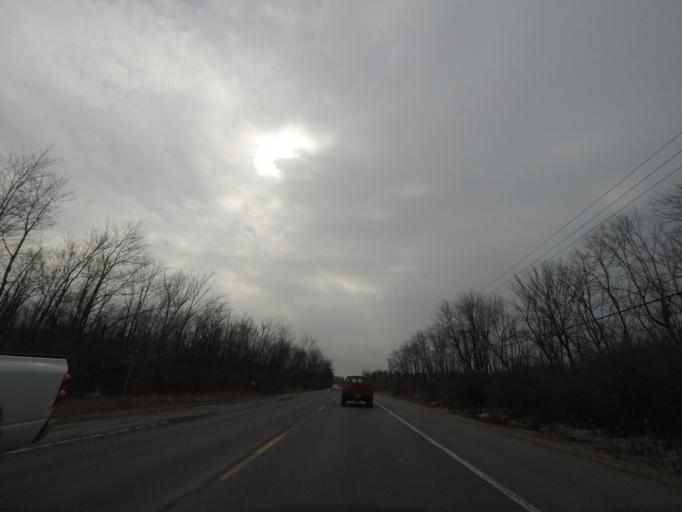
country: US
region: New York
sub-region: Warren County
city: Glens Falls
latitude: 43.3273
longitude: -73.6285
